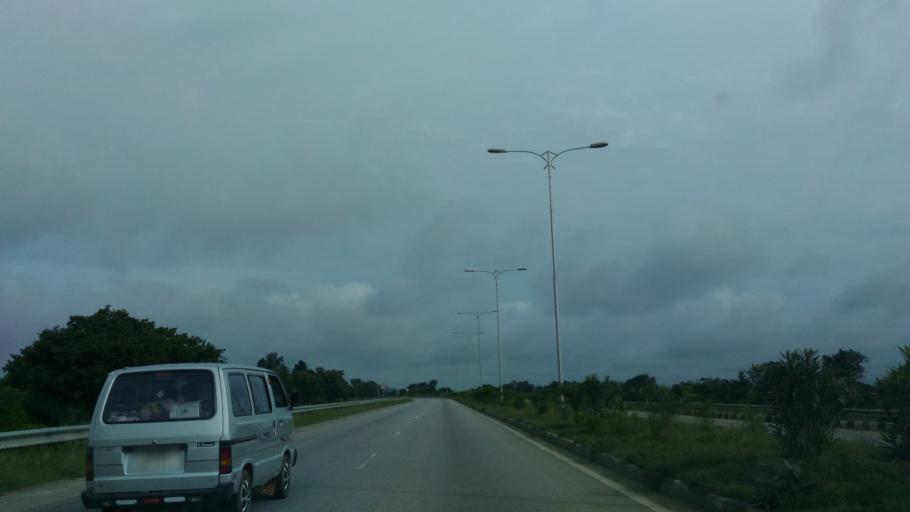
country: IN
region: Karnataka
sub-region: Tumkur
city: Kunigal
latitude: 13.0024
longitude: 77.0175
